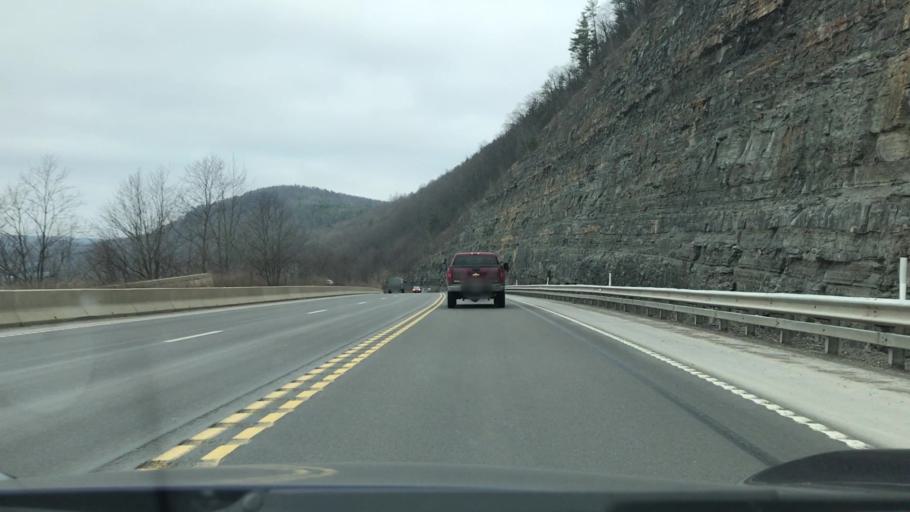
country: US
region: Pennsylvania
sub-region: Bradford County
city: Towanda
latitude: 41.7655
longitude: -76.3693
